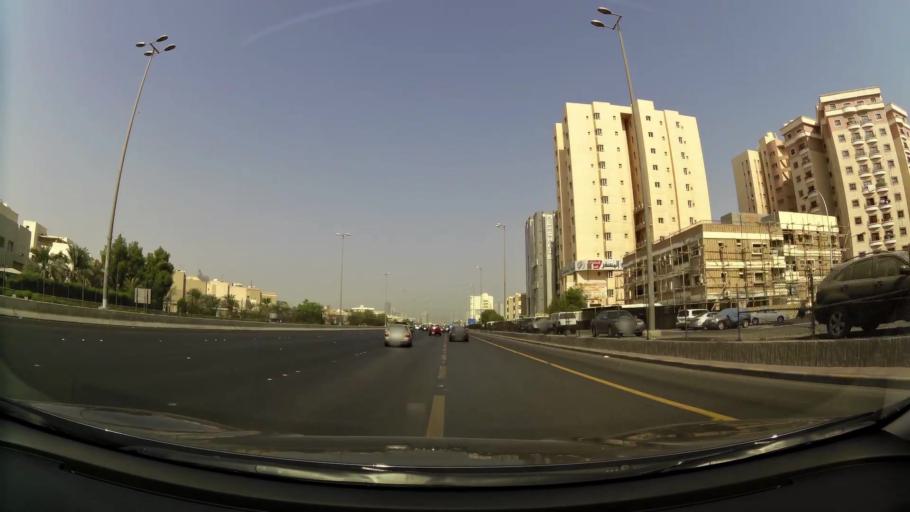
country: KW
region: Muhafazat Hawalli
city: Hawalli
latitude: 29.3336
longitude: 48.0053
